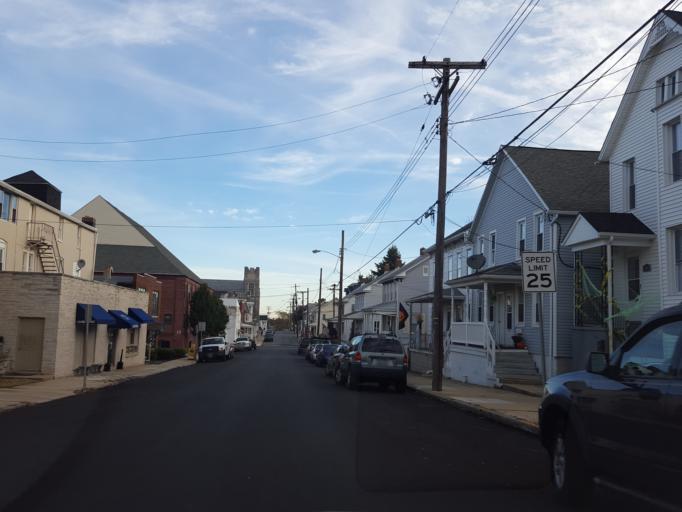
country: US
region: Pennsylvania
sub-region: York County
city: Red Lion
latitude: 39.8993
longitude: -76.6101
